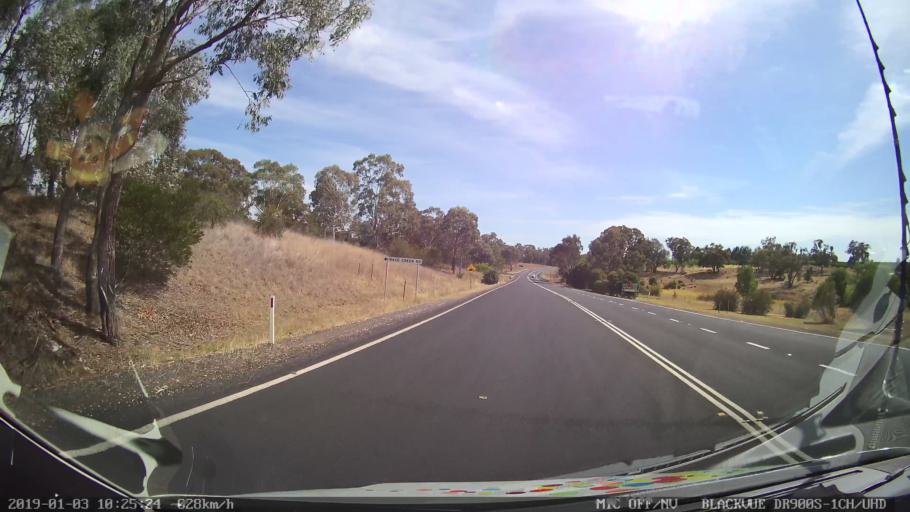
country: AU
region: New South Wales
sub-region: Young
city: Young
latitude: -34.4226
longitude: 148.2441
